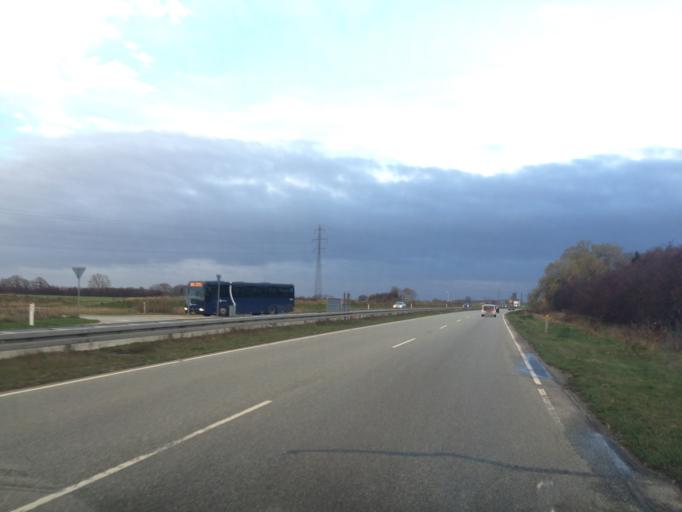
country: DK
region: South Denmark
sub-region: Sonderborg Kommune
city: Augustenborg
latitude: 54.9400
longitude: 9.8769
